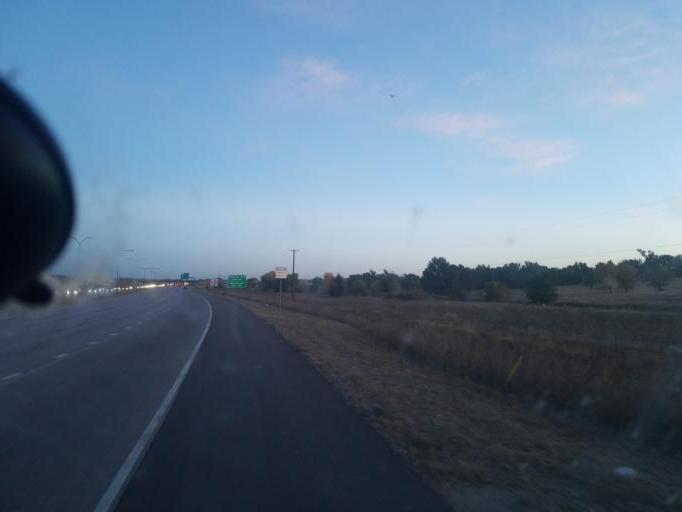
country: US
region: Colorado
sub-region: El Paso County
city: Cimarron Hills
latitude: 38.8313
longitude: -104.7209
